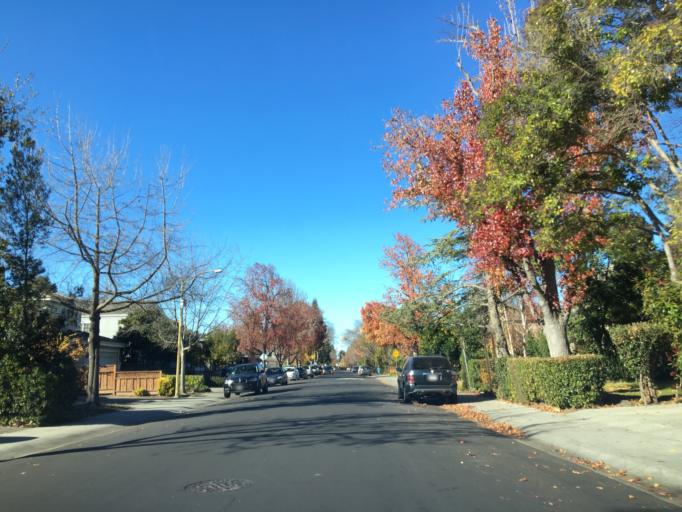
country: US
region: California
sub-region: Santa Clara County
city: Palo Alto
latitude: 37.4222
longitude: -122.1215
